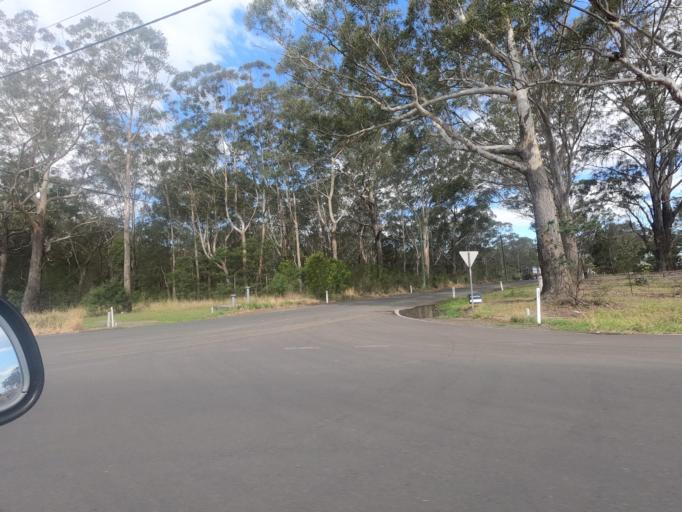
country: AU
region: New South Wales
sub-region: Wollongong
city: Dapto
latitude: -34.4745
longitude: 150.7904
